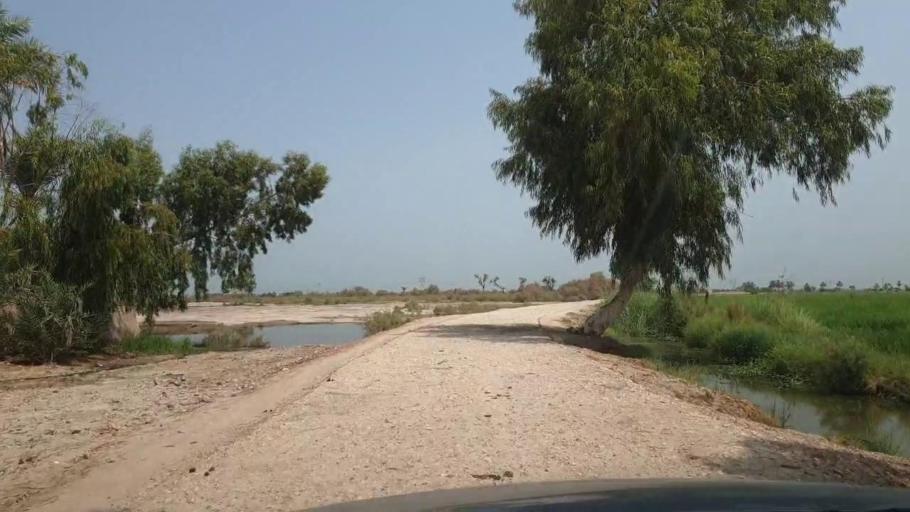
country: PK
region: Sindh
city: Madeji
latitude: 27.8010
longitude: 68.5316
